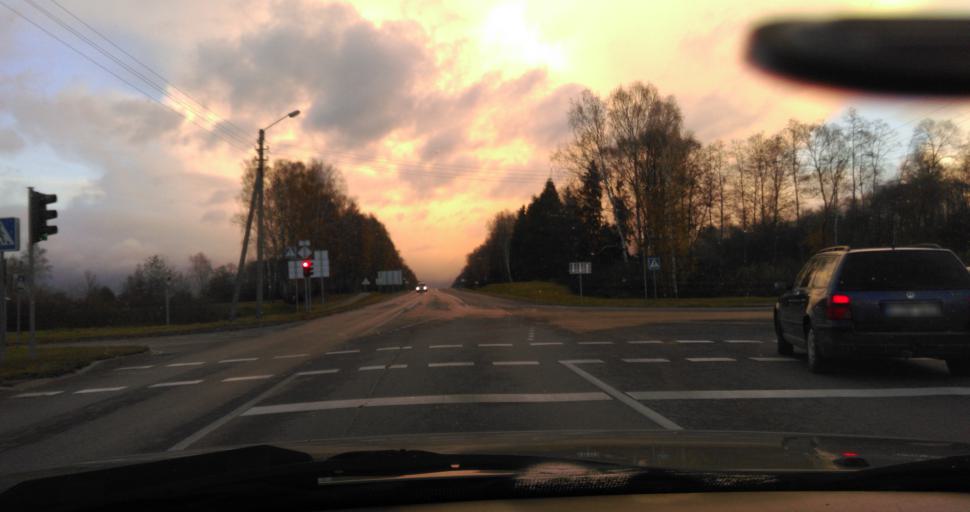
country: LT
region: Utenos apskritis
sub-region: Utena
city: Utena
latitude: 55.5072
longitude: 25.6293
